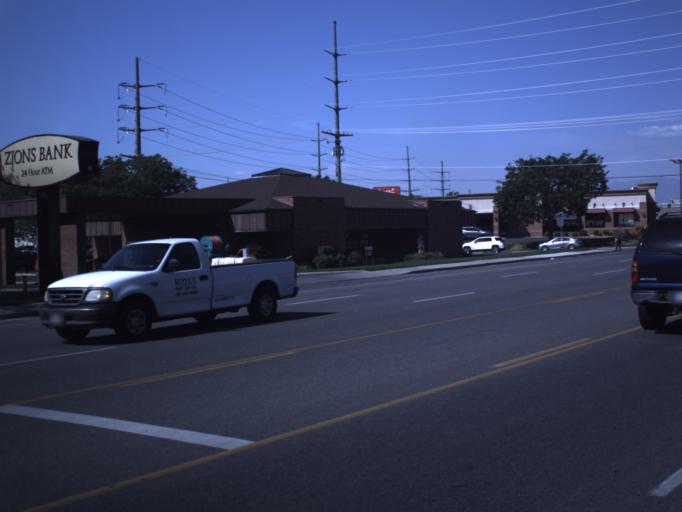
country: US
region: Utah
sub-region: Utah County
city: American Fork
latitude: 40.3731
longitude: -111.7818
